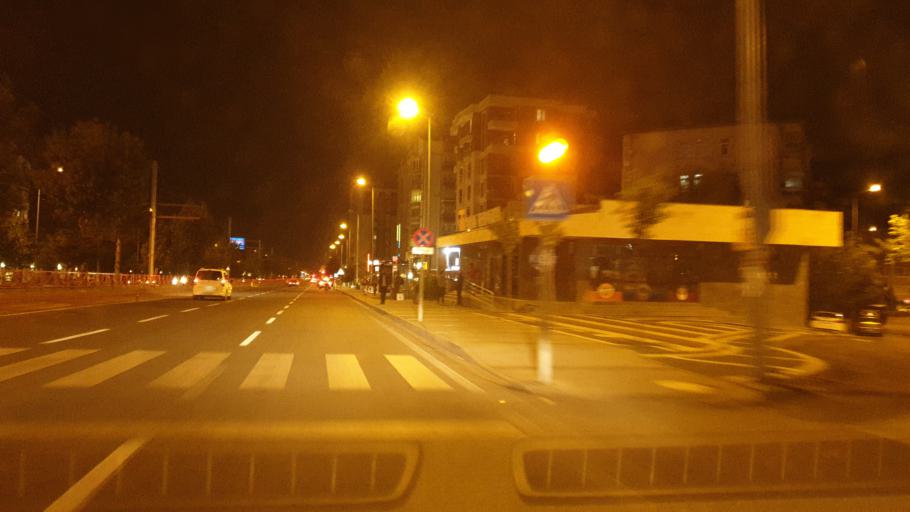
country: TR
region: Kayseri
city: Talas
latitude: 38.6943
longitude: 35.5450
